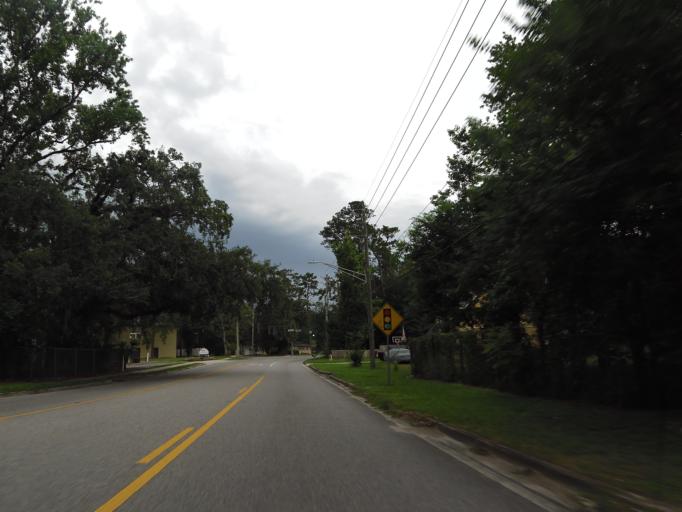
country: US
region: Florida
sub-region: Duval County
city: Jacksonville
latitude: 30.2733
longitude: -81.5910
